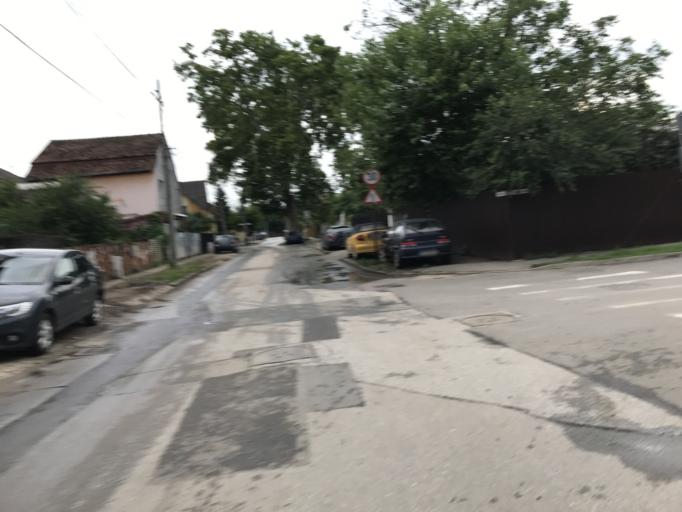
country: RO
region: Timis
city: Timisoara
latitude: 45.7719
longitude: 21.2342
